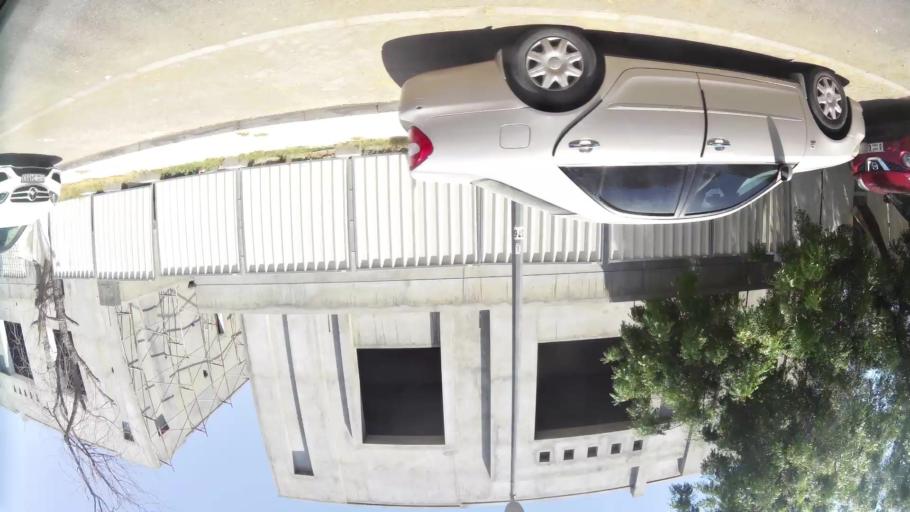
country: AE
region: Ash Shariqah
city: Sharjah
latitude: 25.2881
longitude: 55.3469
